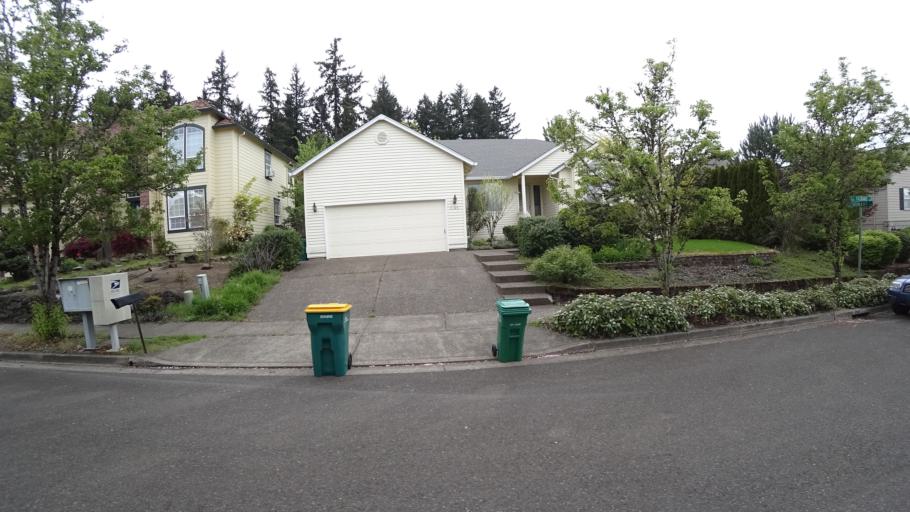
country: US
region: Oregon
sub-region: Washington County
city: Beaverton
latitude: 45.4595
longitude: -122.8170
